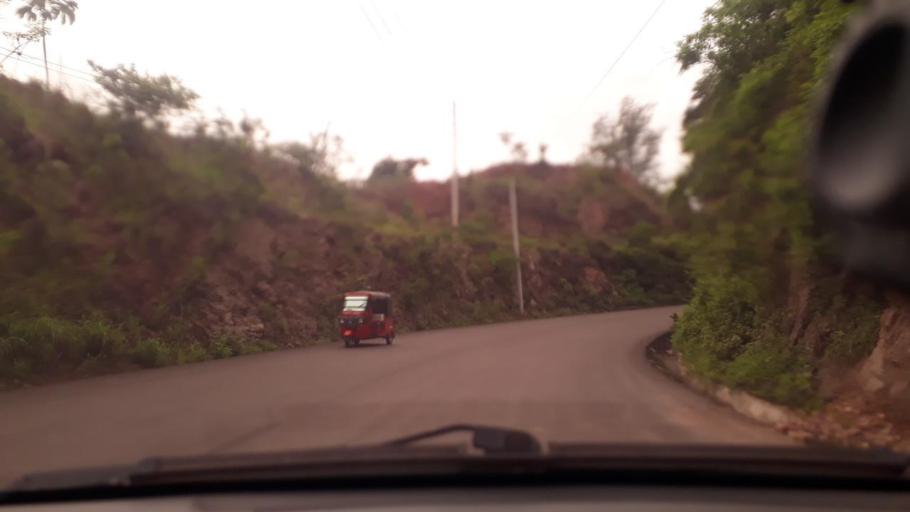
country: GT
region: Chiquimula
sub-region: Municipio de San Juan Ermita
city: San Juan Ermita
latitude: 14.7469
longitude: -89.4643
